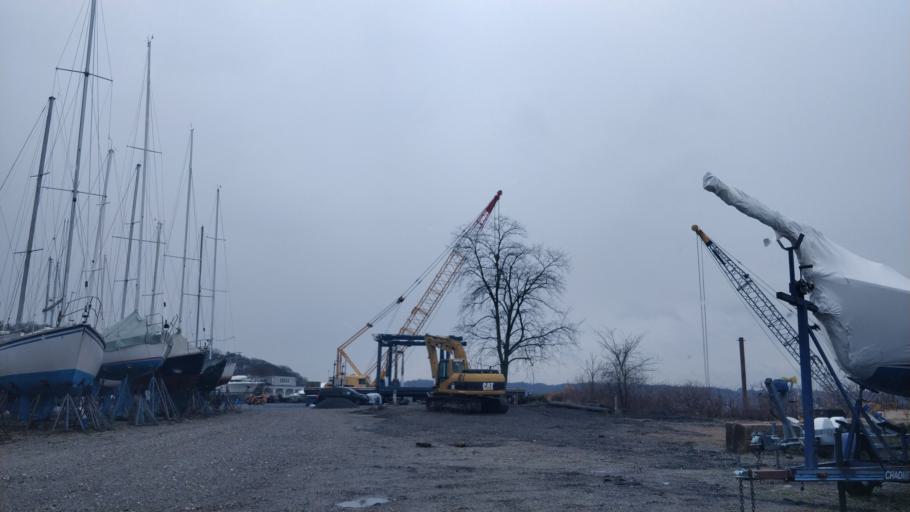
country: US
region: New York
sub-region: Nassau County
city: Sea Cliff
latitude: 40.8568
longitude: -73.6441
